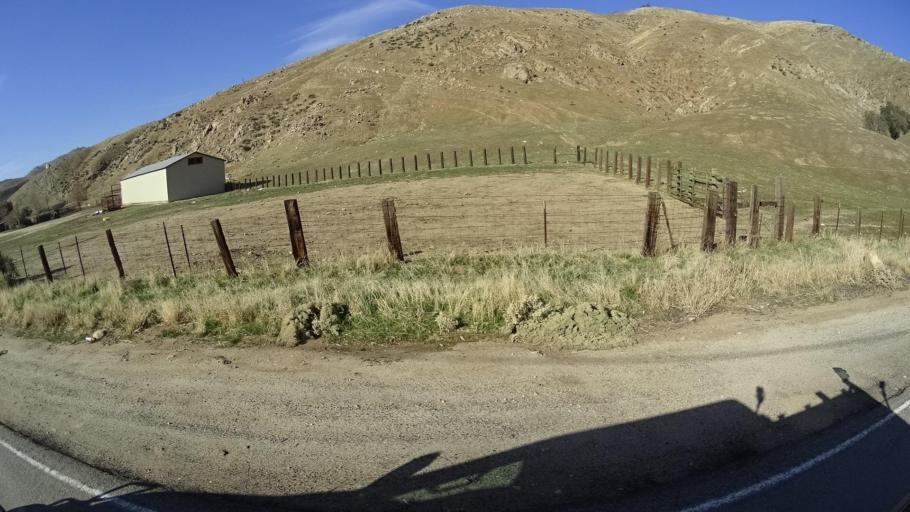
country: US
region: California
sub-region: Kern County
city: Bear Valley Springs
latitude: 35.2972
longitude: -118.6096
